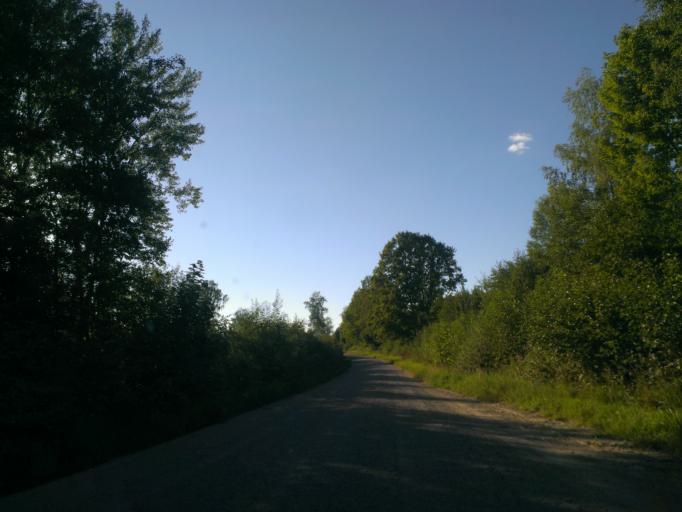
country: LV
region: Malpils
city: Malpils
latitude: 57.0850
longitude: 25.0550
